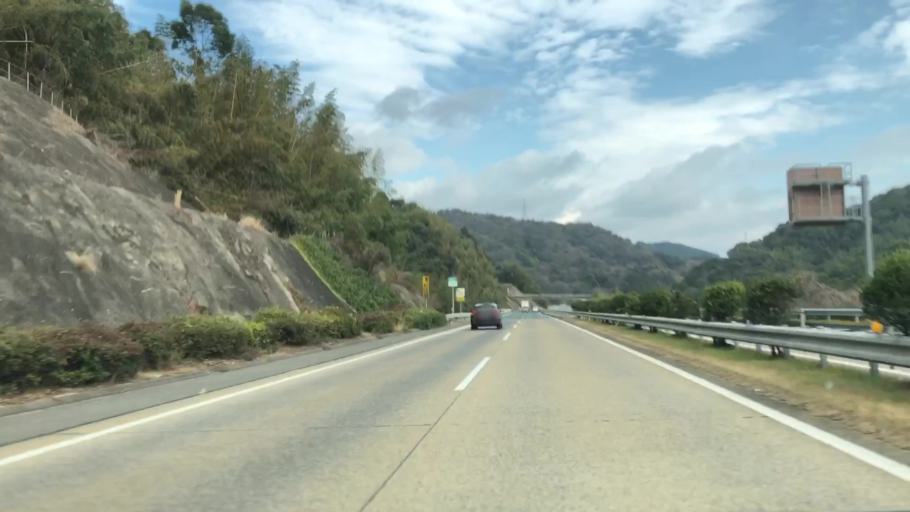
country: JP
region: Saga Prefecture
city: Kanzakimachi-kanzaki
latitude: 33.3348
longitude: 130.3258
